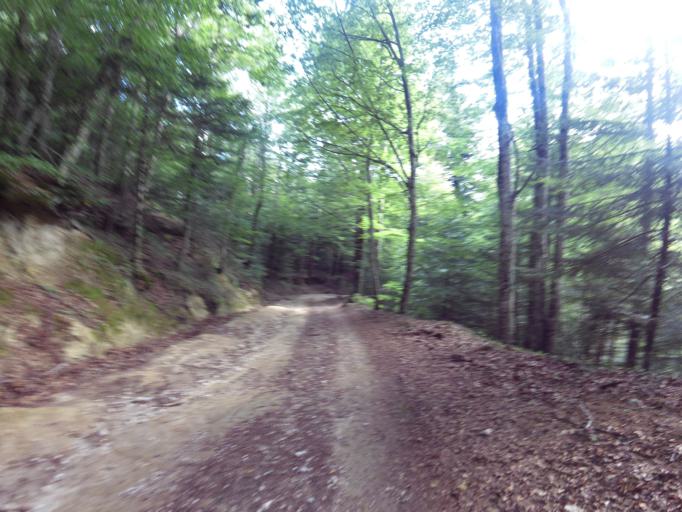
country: IT
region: Calabria
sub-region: Provincia di Vibo-Valentia
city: Mongiana
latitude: 38.5278
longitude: 16.3779
